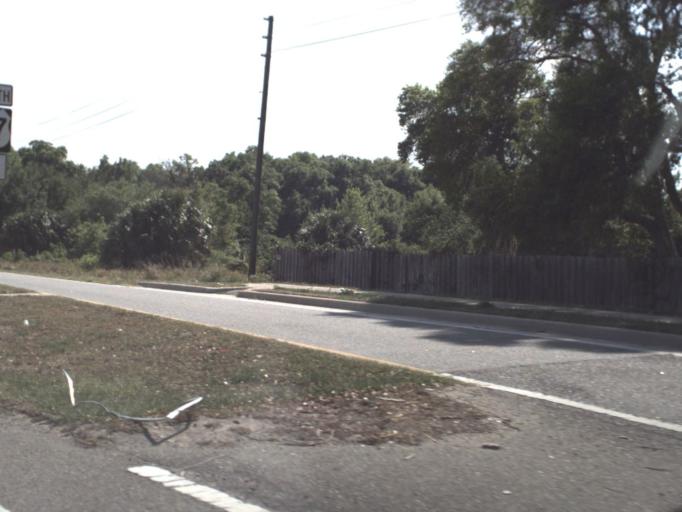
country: US
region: Florida
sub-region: Lake County
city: Minneola
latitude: 28.5841
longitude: -81.7520
